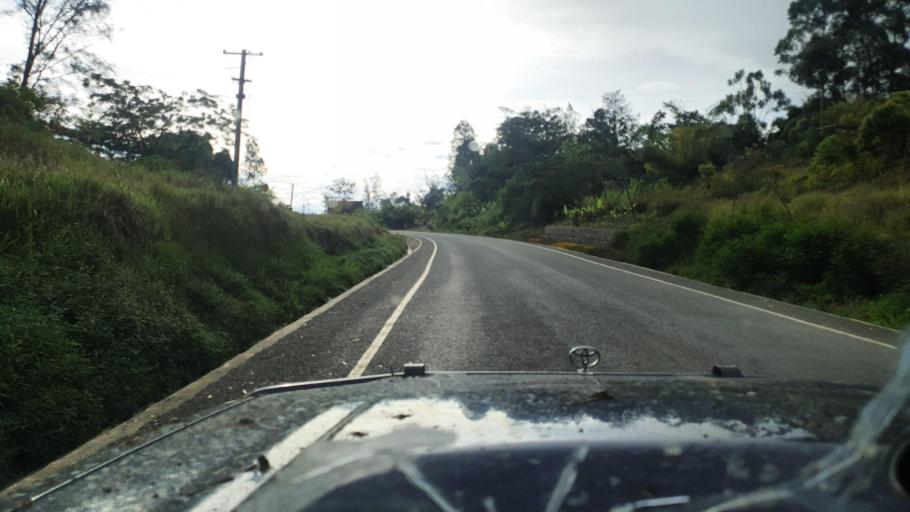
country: PG
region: Jiwaka
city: Minj
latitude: -5.9302
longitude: 144.7985
